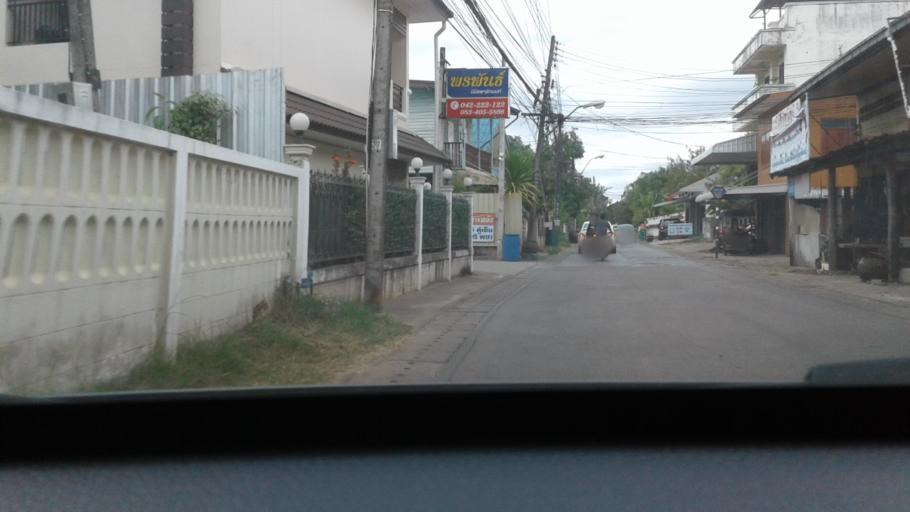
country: TH
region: Changwat Udon Thani
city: Udon Thani
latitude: 17.3996
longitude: 102.7798
